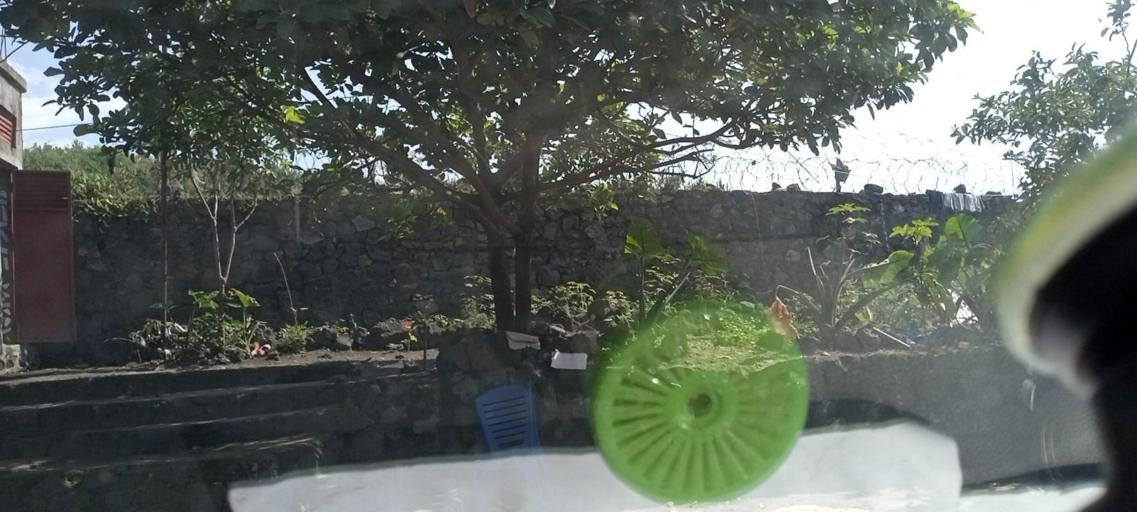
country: CD
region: Nord Kivu
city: Goma
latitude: -1.6789
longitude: 29.2202
